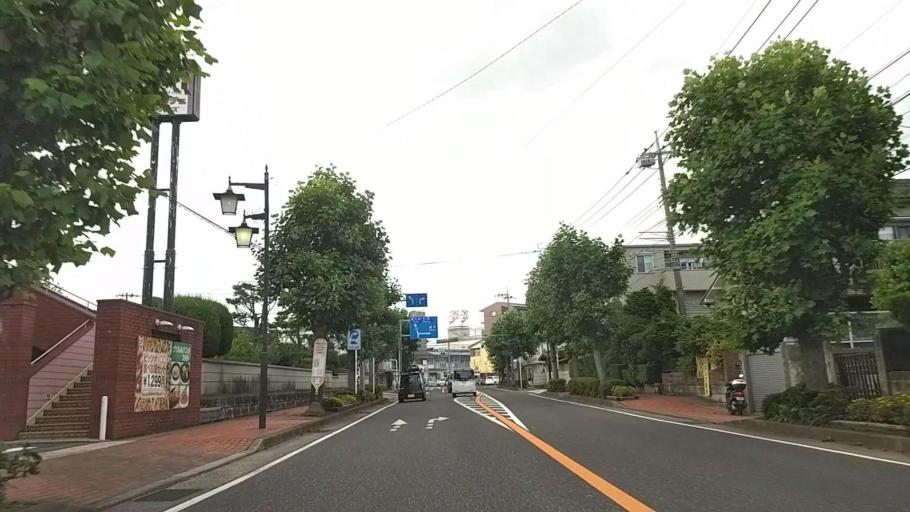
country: JP
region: Kanagawa
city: Isehara
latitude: 35.3916
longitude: 139.3145
